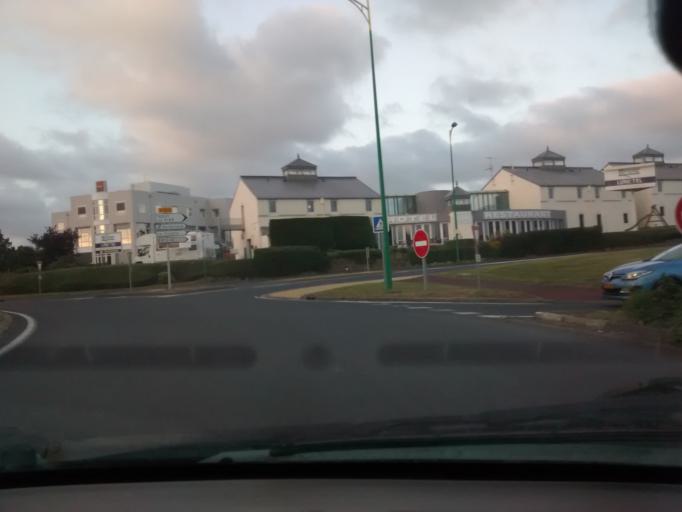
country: FR
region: Lower Normandy
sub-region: Departement de la Manche
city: Agneaux
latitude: 49.1010
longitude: -1.1158
